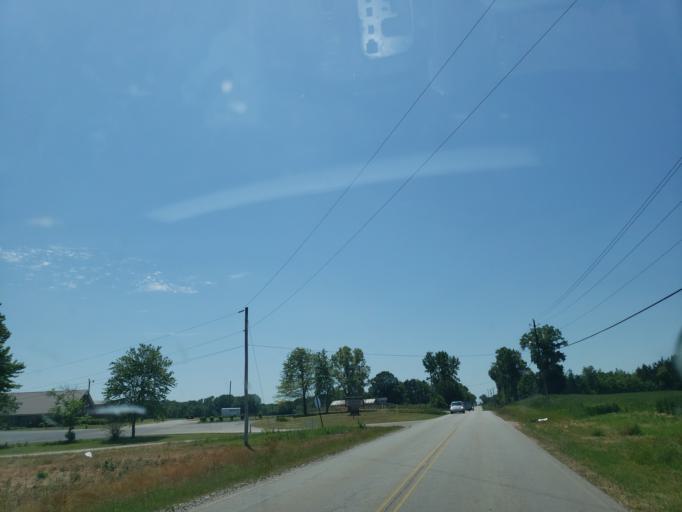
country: US
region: Alabama
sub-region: Madison County
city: Harvest
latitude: 34.8915
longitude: -86.7362
